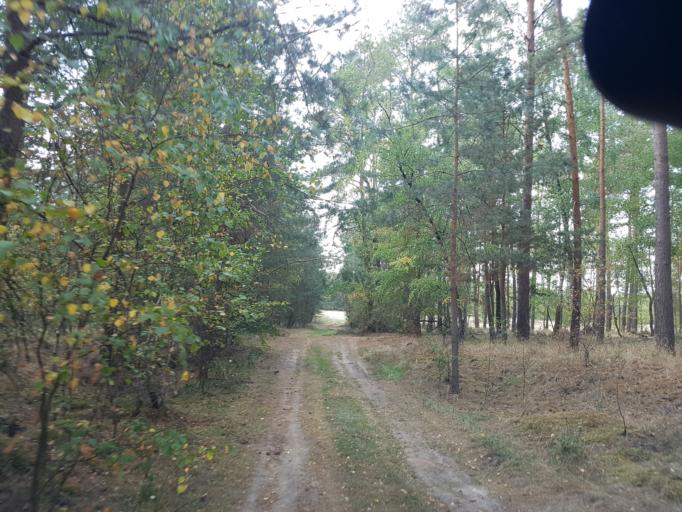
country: DE
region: Brandenburg
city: Treuenbrietzen
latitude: 52.0207
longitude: 12.8722
